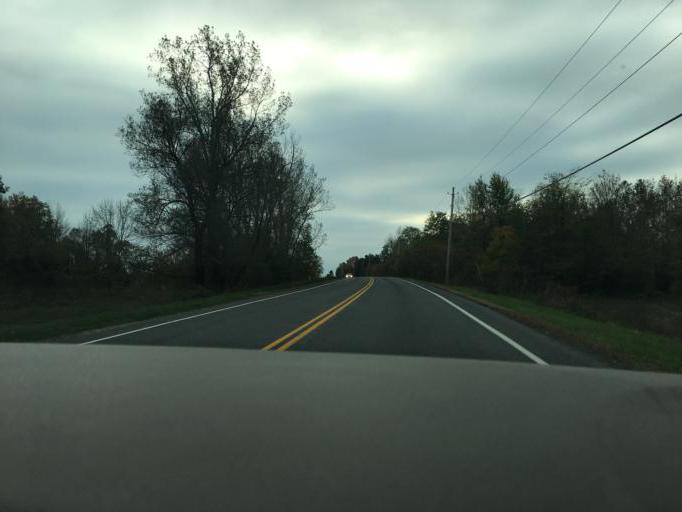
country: US
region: New York
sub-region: Wayne County
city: Macedon
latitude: 43.0253
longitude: -77.3229
